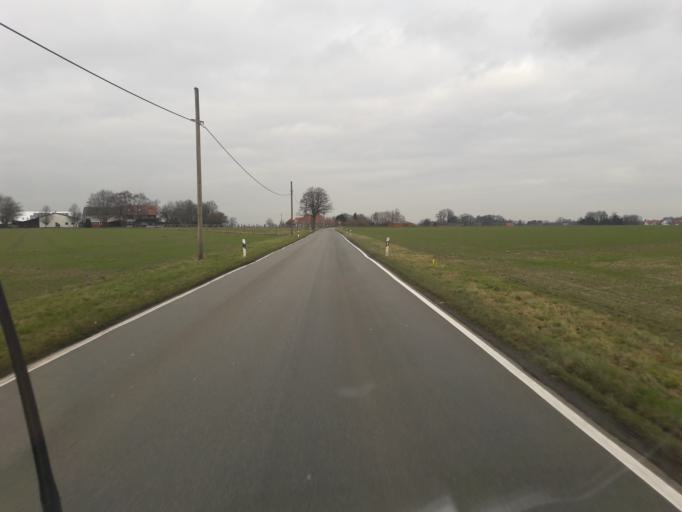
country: DE
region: North Rhine-Westphalia
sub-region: Regierungsbezirk Detmold
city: Hille
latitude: 52.3224
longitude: 8.8313
